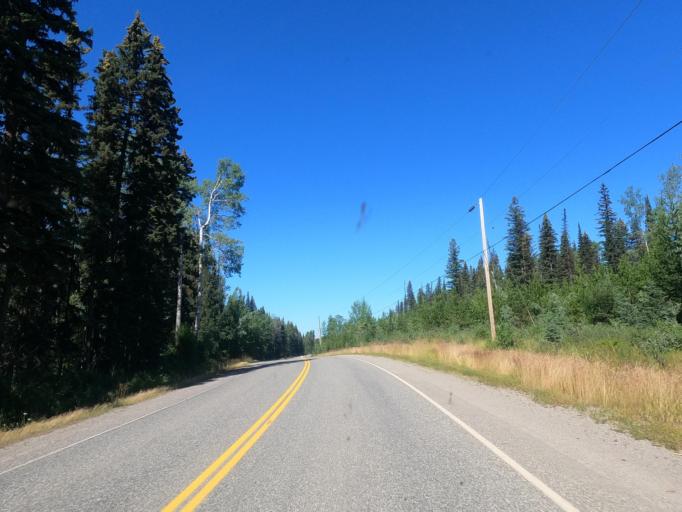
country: CA
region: British Columbia
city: Quesnel
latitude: 53.0278
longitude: -122.0942
